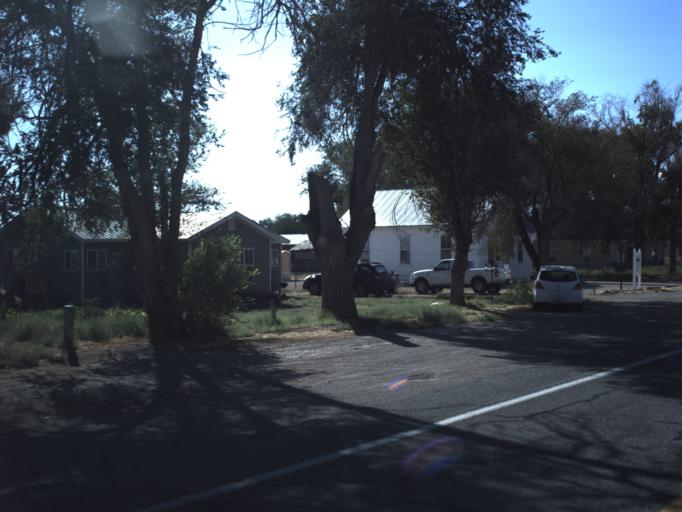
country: US
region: Utah
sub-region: Millard County
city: Delta
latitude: 39.2896
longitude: -112.6527
